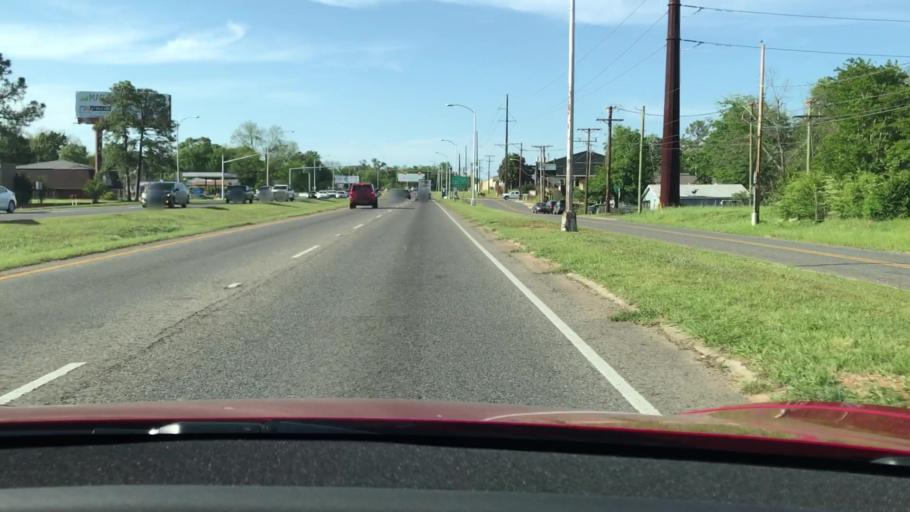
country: US
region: Louisiana
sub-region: Bossier Parish
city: Bossier City
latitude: 32.4984
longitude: -93.7248
